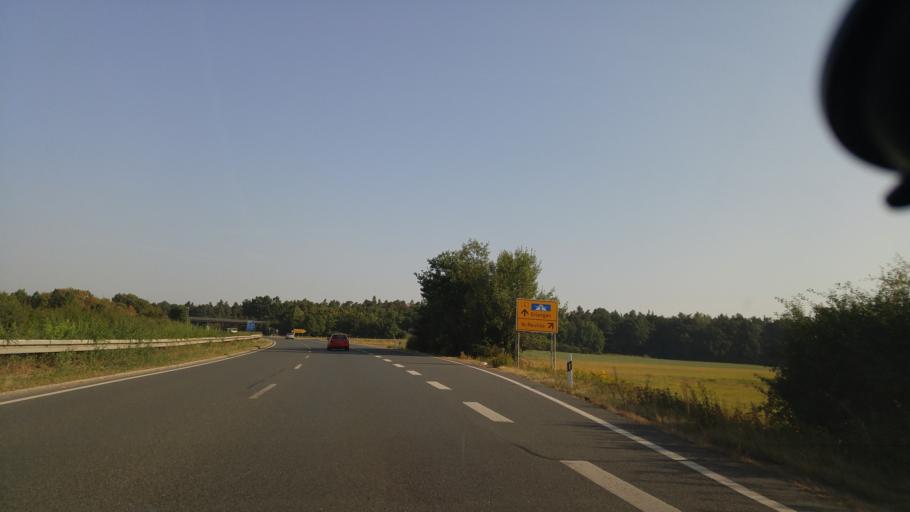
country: DE
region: Bavaria
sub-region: Regierungsbezirk Mittelfranken
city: Wetzendorf
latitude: 49.5288
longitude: 11.0327
